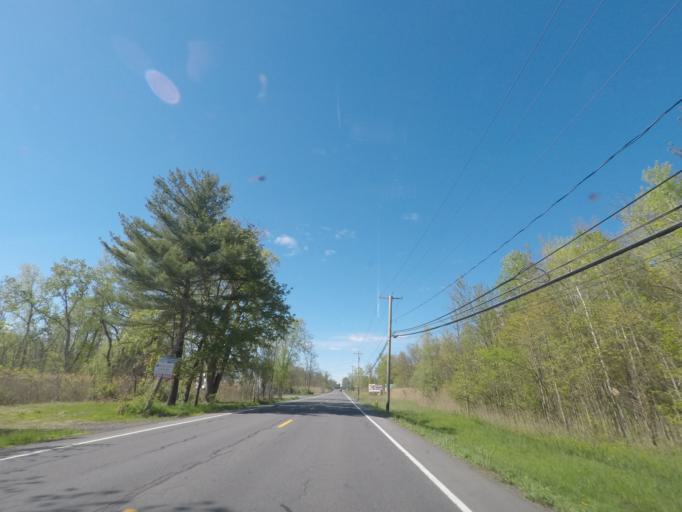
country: US
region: New York
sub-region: Rensselaer County
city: Castleton-on-Hudson
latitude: 42.5444
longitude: -73.8066
